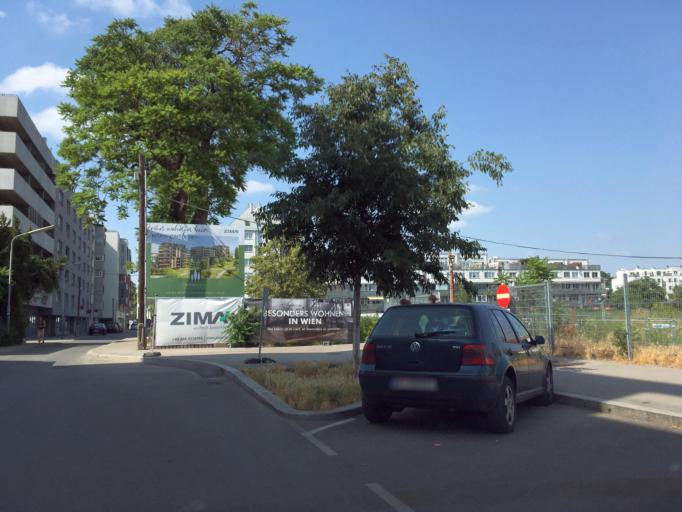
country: AT
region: Lower Austria
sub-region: Politischer Bezirk Wien-Umgebung
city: Gerasdorf bei Wien
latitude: 48.2491
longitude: 16.4344
